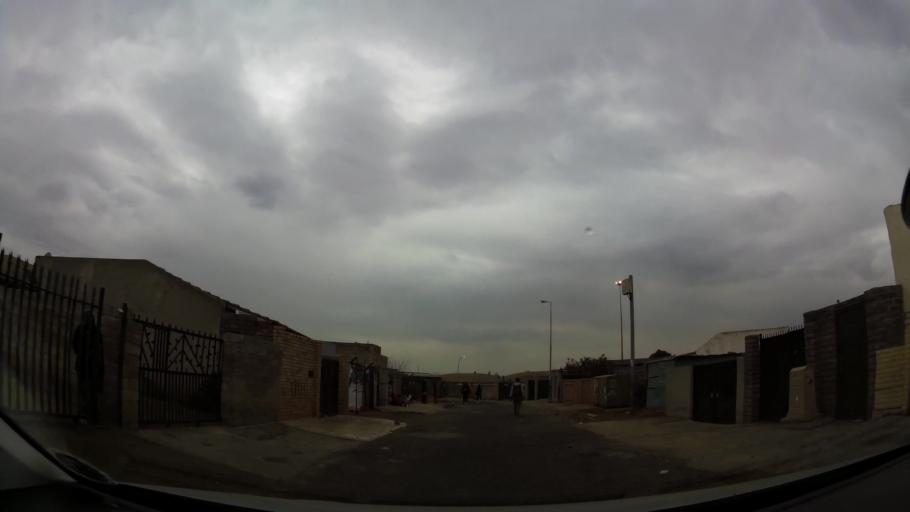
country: ZA
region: Gauteng
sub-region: City of Johannesburg Metropolitan Municipality
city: Soweto
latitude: -26.2553
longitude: 27.8728
